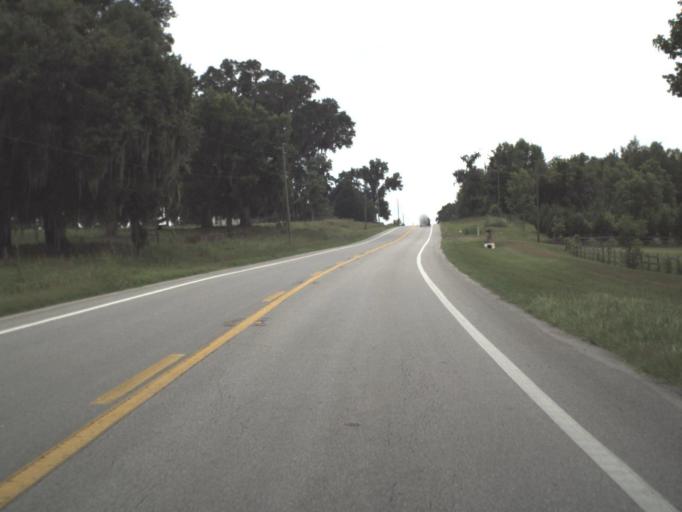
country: US
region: Florida
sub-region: Madison County
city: Madison
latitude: 30.5138
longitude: -83.4226
